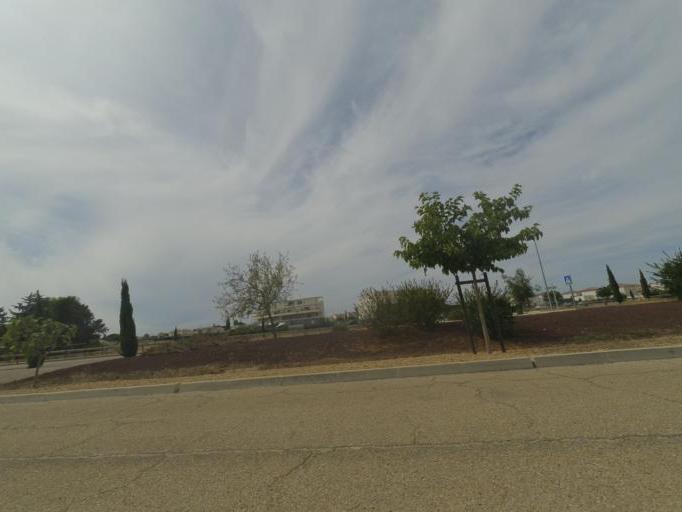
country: FR
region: Languedoc-Roussillon
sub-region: Departement du Gard
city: Aimargues
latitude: 43.6985
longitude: 4.2048
